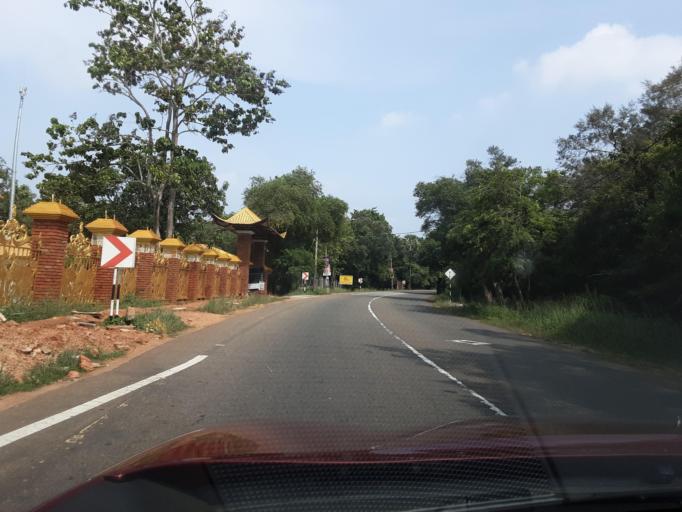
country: LK
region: North Central
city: Anuradhapura
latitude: 8.3453
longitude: 80.5057
